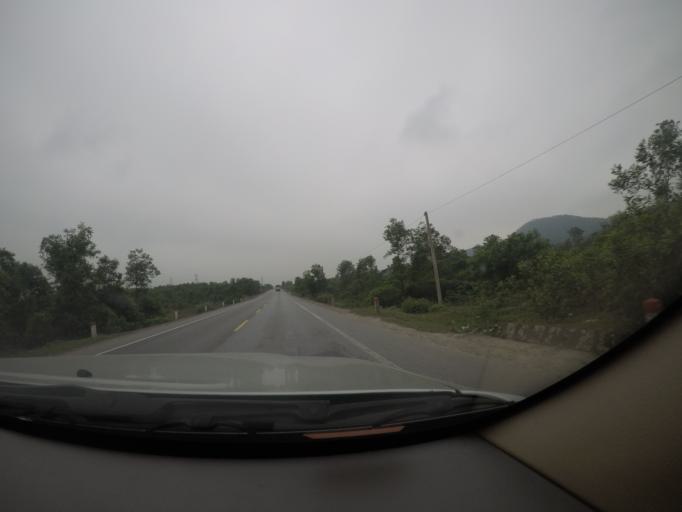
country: VN
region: Ha Tinh
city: Ky Anh
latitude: 18.0280
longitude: 106.3326
